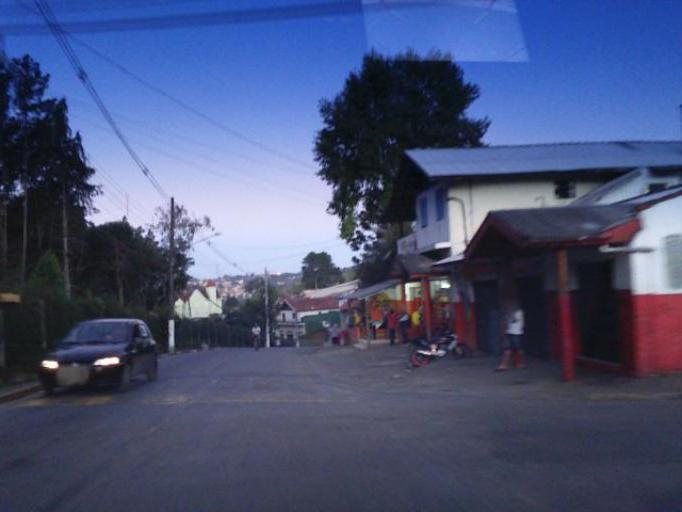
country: BR
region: Sao Paulo
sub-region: Campos Do Jordao
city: Campos do Jordao
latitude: -22.7377
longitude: -45.6028
